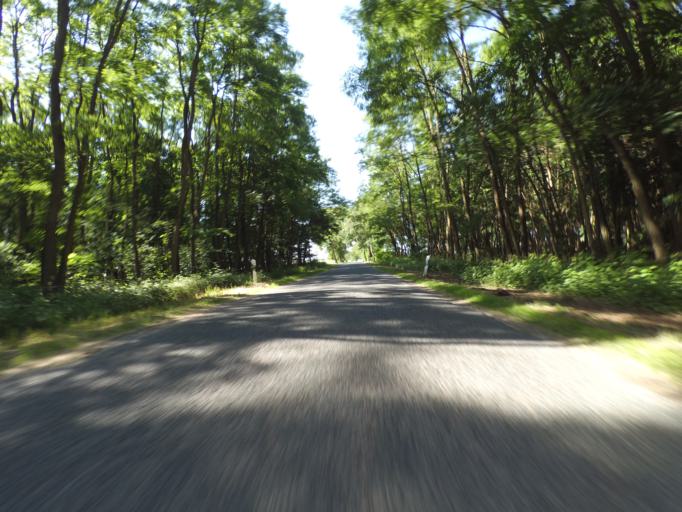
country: DE
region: Brandenburg
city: Triglitz
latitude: 53.2489
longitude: 12.1242
